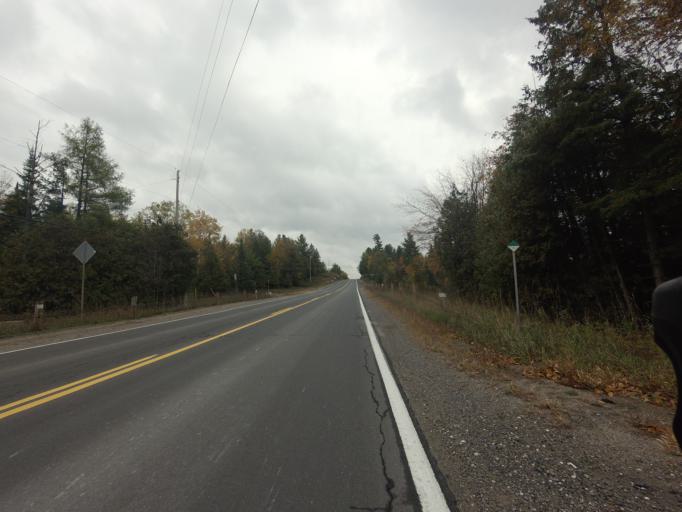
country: CA
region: Ontario
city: Perth
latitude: 45.1109
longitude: -76.4814
